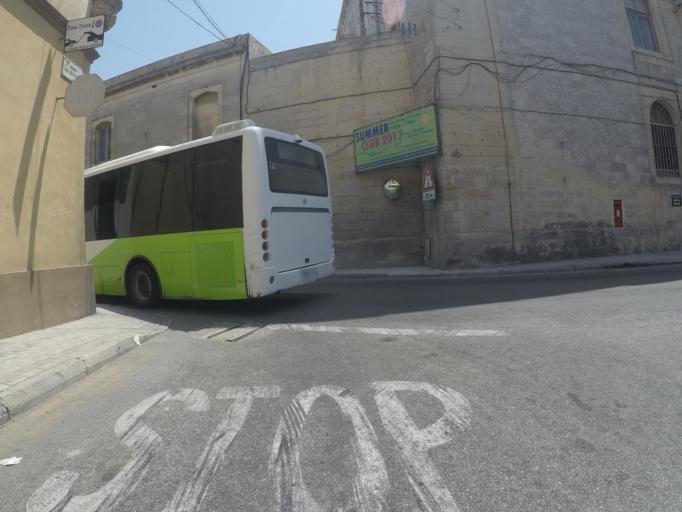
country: MT
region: Ir-Rabat
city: Rabat
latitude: 35.8768
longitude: 14.3991
